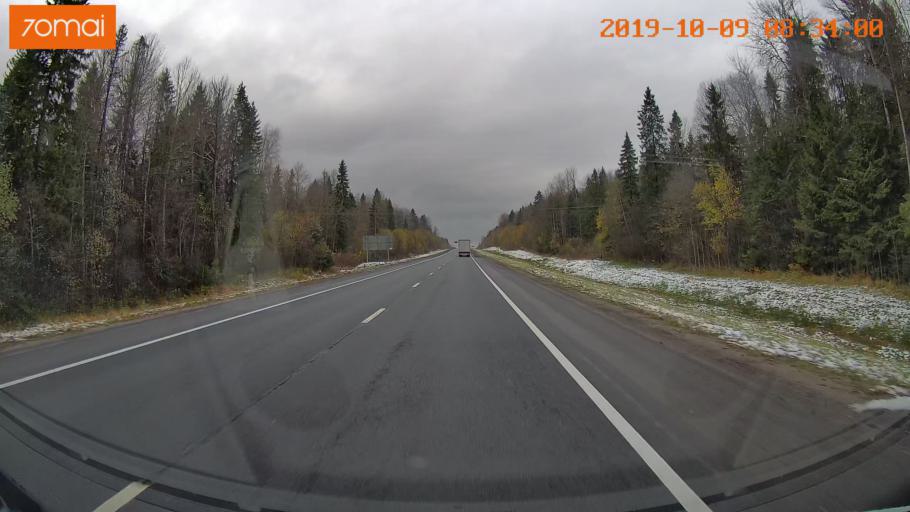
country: RU
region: Vologda
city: Gryazovets
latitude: 58.8905
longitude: 40.1885
